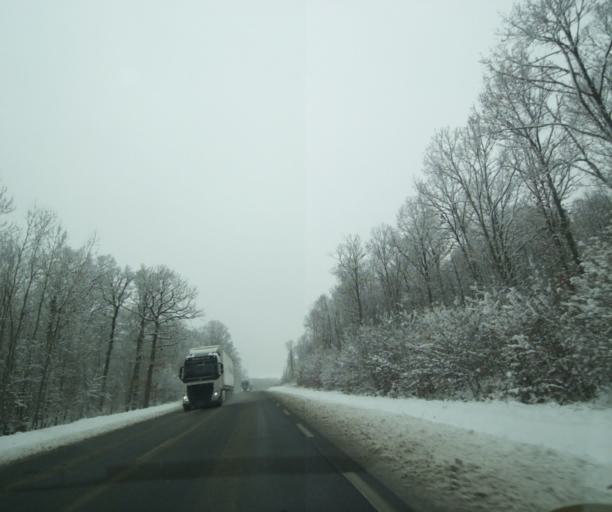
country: FR
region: Champagne-Ardenne
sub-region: Departement de la Haute-Marne
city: Laneuville-a-Remy
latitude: 48.5492
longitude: 4.8344
